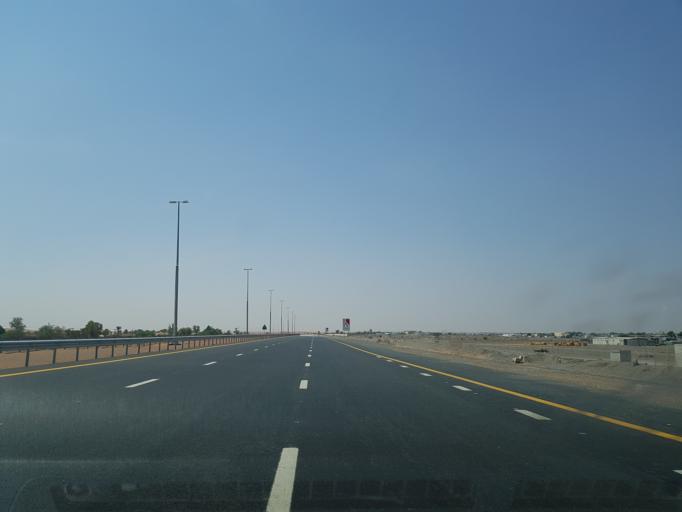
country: AE
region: Ash Shariqah
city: Adh Dhayd
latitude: 25.2335
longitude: 55.9089
